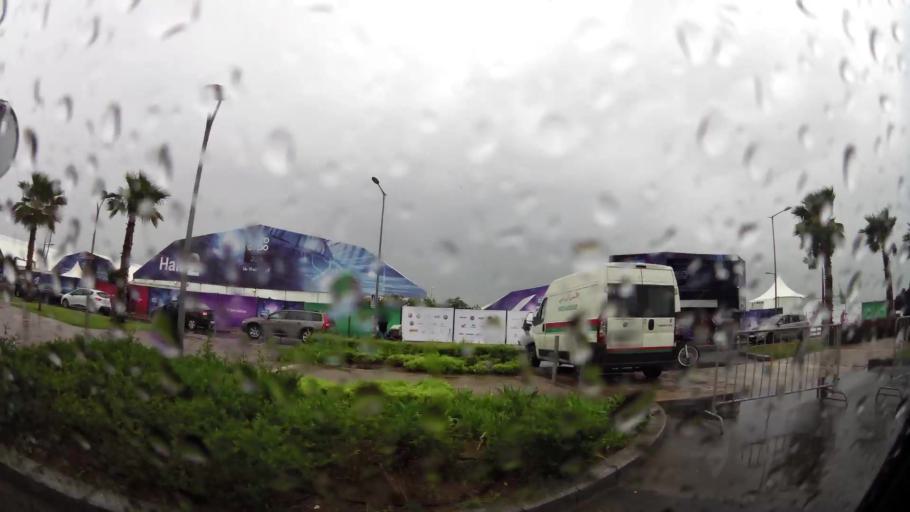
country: MA
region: Grand Casablanca
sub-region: Casablanca
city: Casablanca
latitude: 33.5500
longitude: -7.6668
